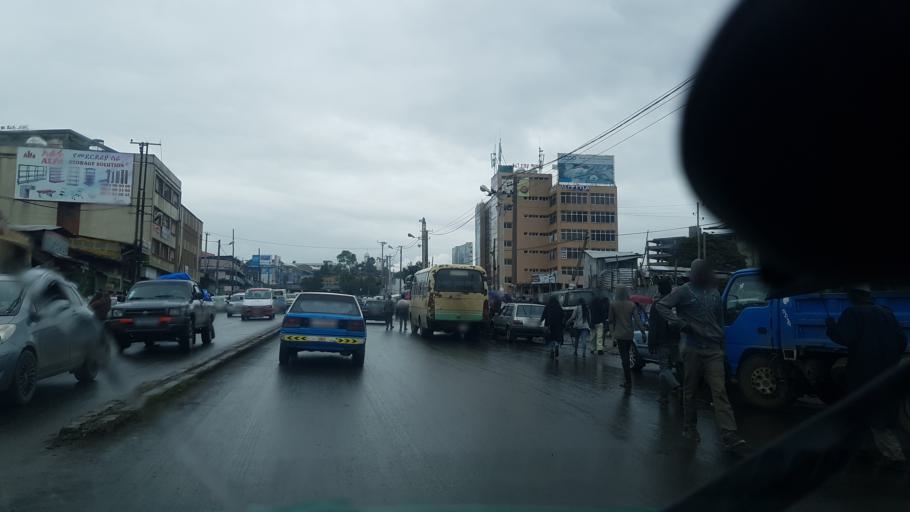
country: ET
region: Adis Abeba
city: Addis Ababa
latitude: 9.0293
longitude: 38.7428
